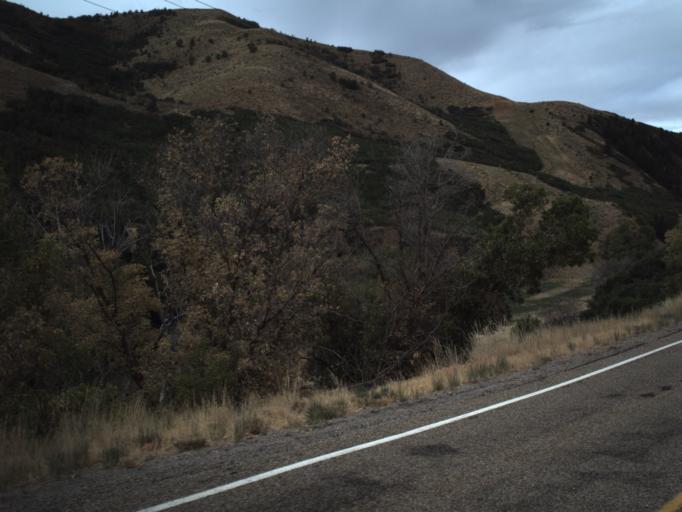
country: US
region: Utah
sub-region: Morgan County
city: Morgan
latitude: 40.9354
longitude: -111.6313
